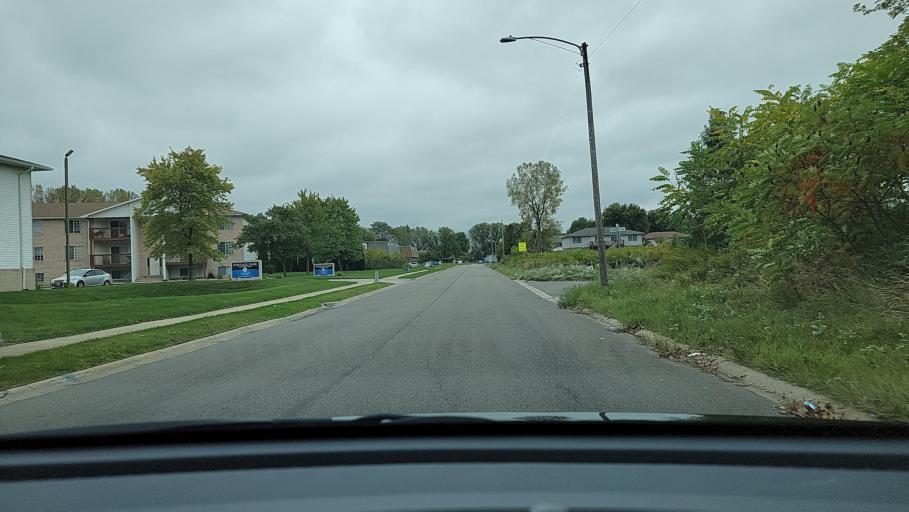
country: US
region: Indiana
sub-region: Porter County
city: Portage
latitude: 41.5494
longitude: -87.1882
